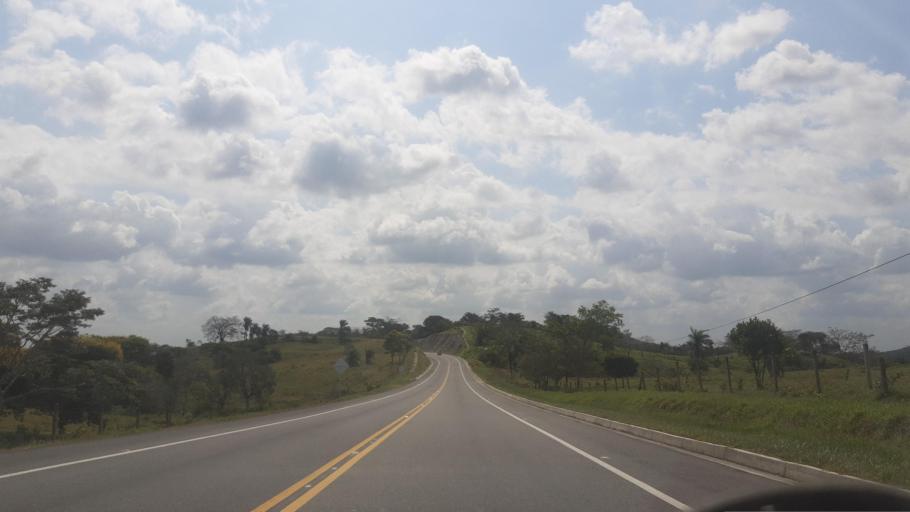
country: CO
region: Casanare
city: Monterrey
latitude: 4.8271
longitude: -72.8104
